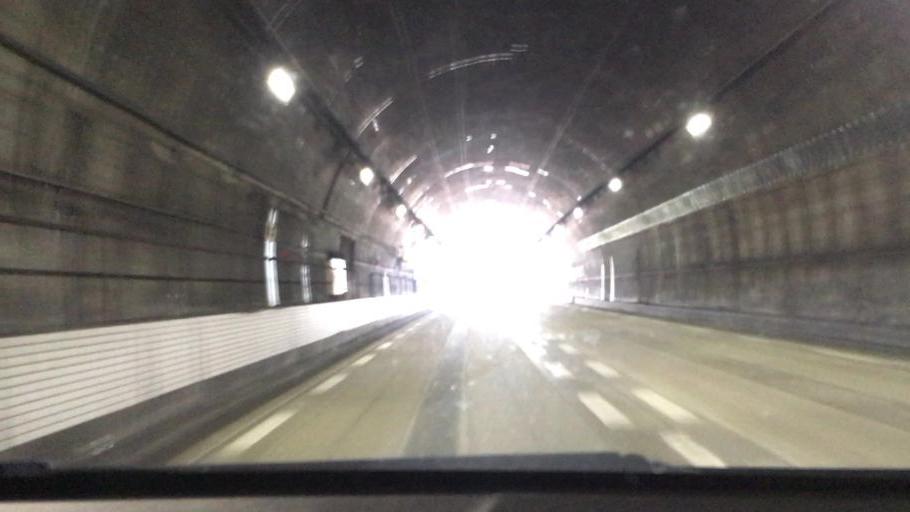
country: JP
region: Yamaguchi
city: Hofu
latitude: 34.0563
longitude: 131.6188
